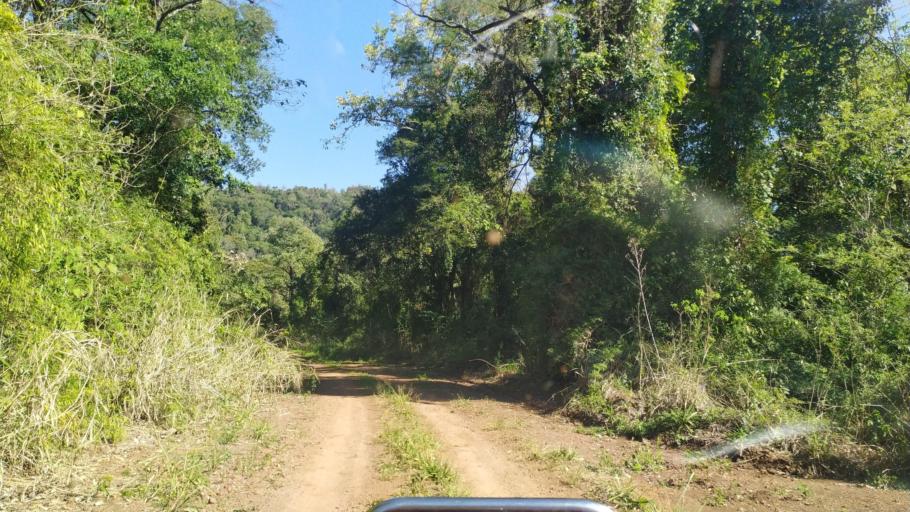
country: AR
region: Misiones
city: El Alcazar
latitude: -26.7586
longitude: -54.5812
